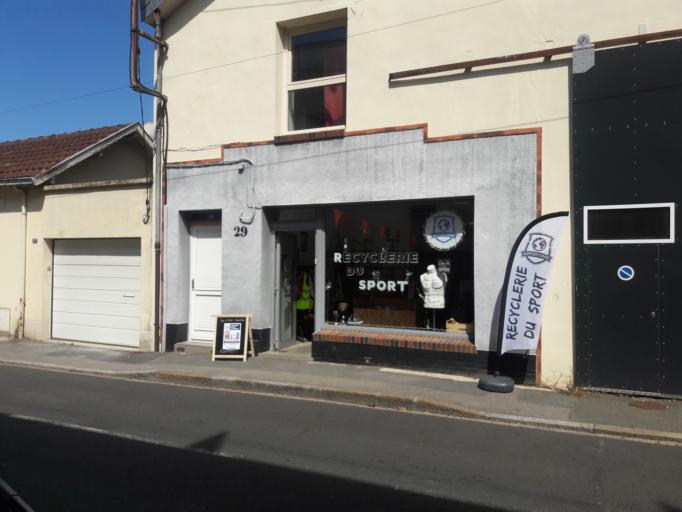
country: FR
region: Pays de la Loire
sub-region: Departement de la Loire-Atlantique
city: Saint-Sebastien-sur-Loire
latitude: 47.2275
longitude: -1.5200
